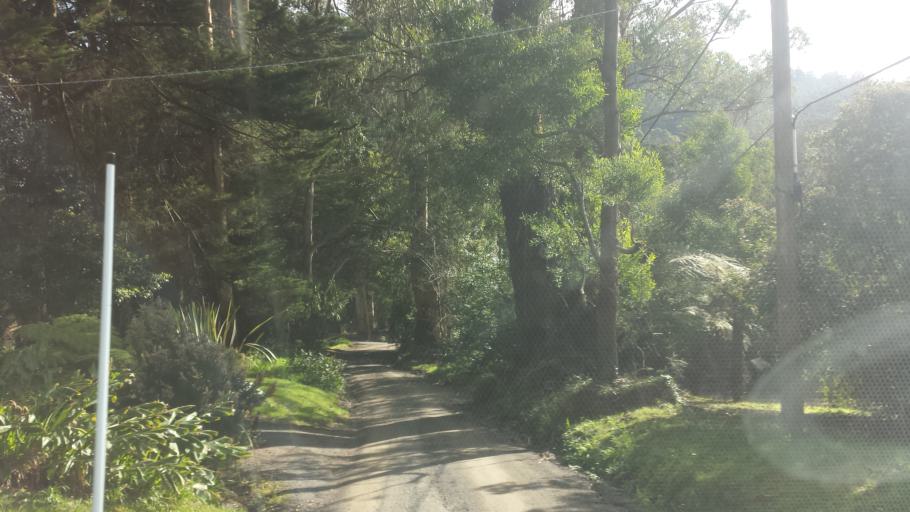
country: AU
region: Victoria
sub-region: Yarra Ranges
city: Kallista
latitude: -37.8820
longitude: 145.3742
